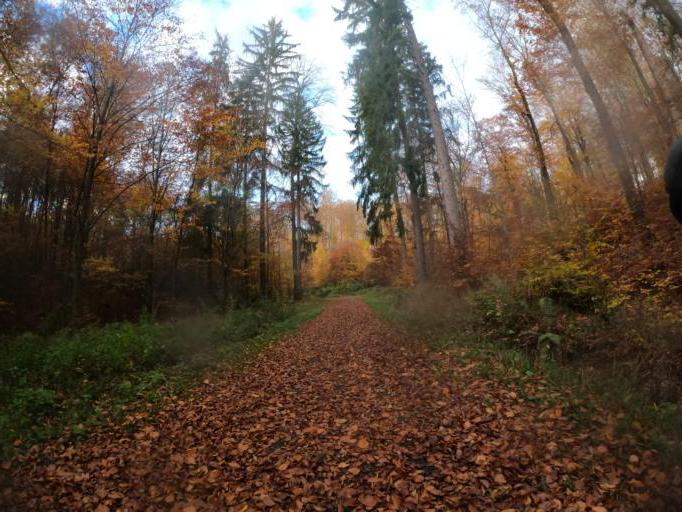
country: DE
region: Baden-Wuerttemberg
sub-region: Regierungsbezirk Stuttgart
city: Sindelfingen
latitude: 48.7165
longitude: 9.0314
